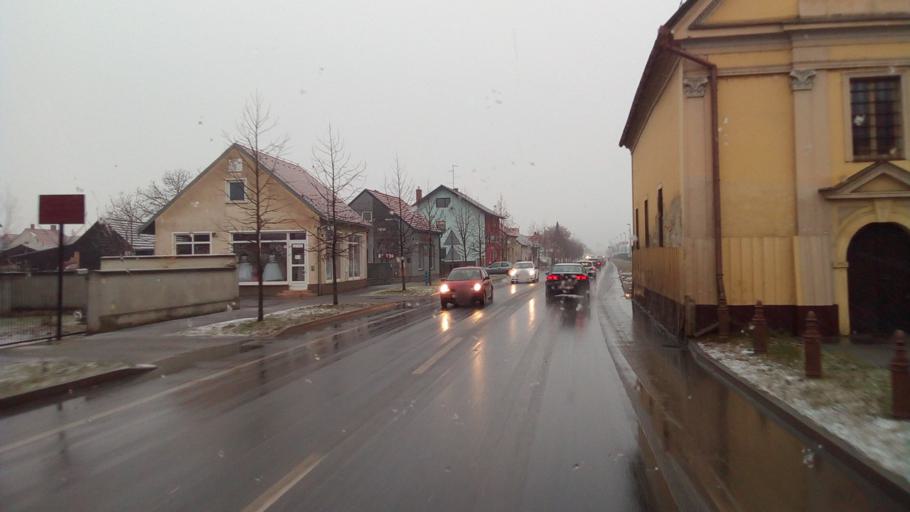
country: HR
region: Varazdinska
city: Varazdin
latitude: 46.3160
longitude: 16.3218
